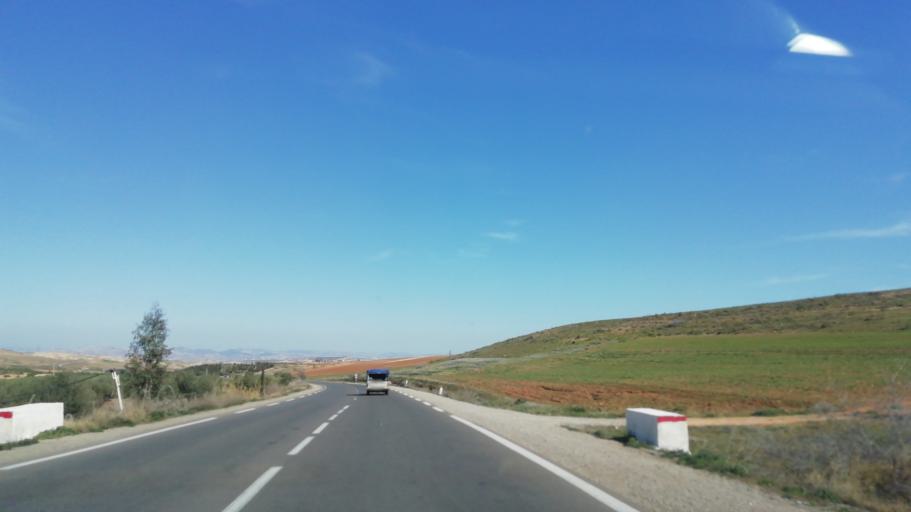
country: DZ
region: Mascara
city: Oued el Abtal
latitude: 35.4314
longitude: 0.4856
